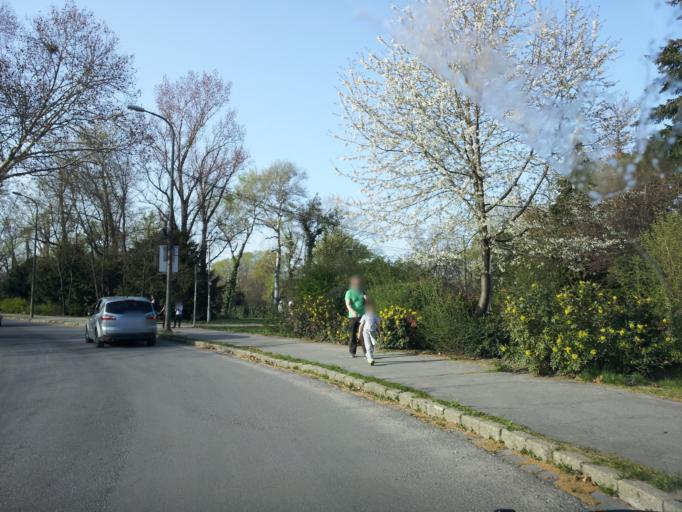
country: HU
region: Budapest
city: Budapest III. keruelet
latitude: 47.5500
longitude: 19.0513
